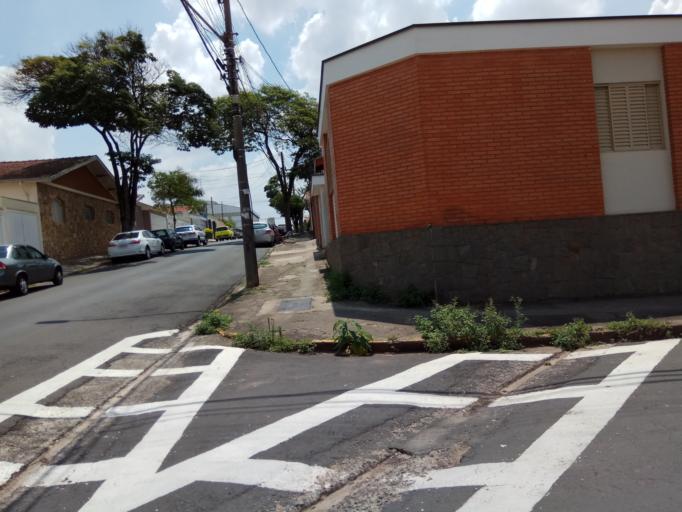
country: BR
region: Sao Paulo
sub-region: Piracicaba
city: Piracicaba
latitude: -22.7153
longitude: -47.6426
